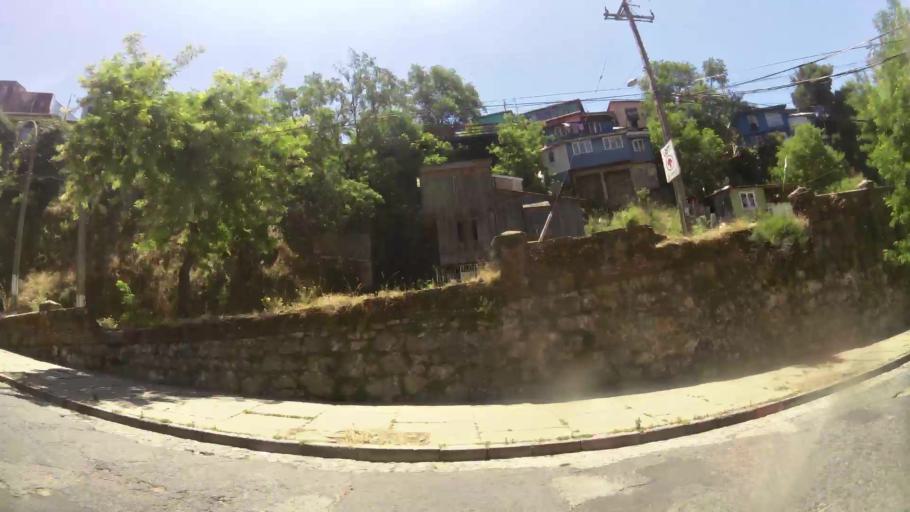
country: CL
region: Valparaiso
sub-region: Provincia de Valparaiso
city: Valparaiso
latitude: -33.0476
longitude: -71.6277
